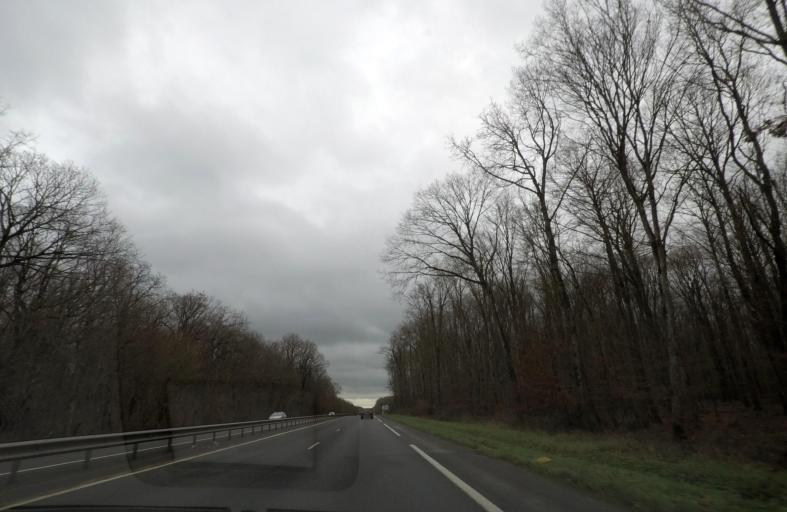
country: FR
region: Centre
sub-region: Departement du Loir-et-Cher
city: Cellettes
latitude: 47.5471
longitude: 1.3954
